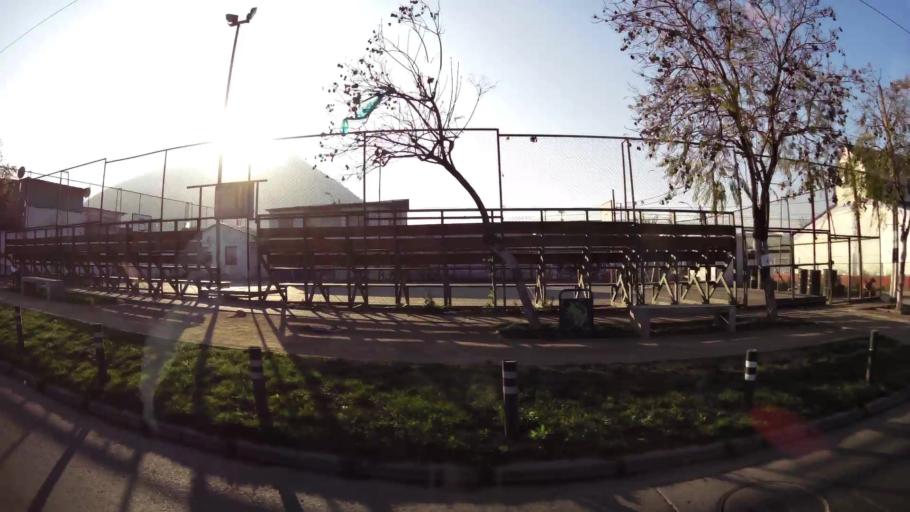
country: CL
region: Santiago Metropolitan
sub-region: Provincia de Santiago
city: Santiago
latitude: -33.3720
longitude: -70.6359
